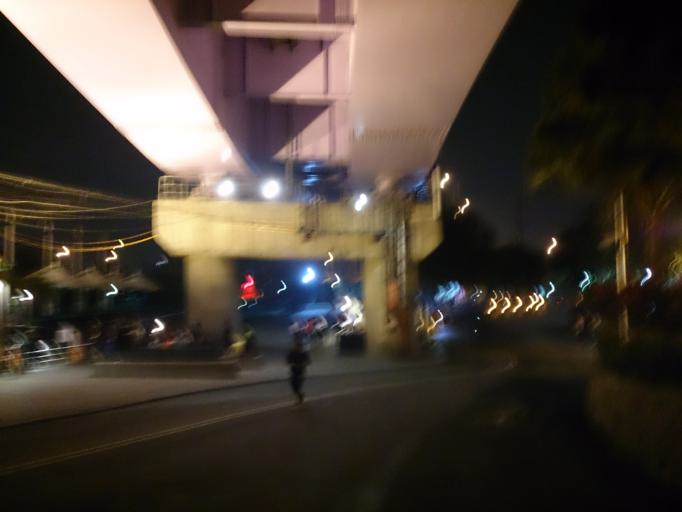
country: TW
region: Taipei
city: Taipei
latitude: 25.0107
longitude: 121.5292
